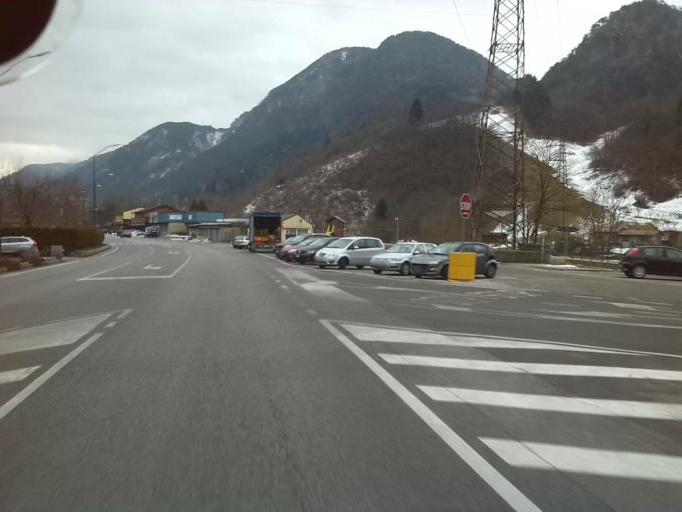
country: IT
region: Friuli Venezia Giulia
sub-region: Provincia di Udine
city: Resiutta
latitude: 46.3938
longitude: 13.2213
